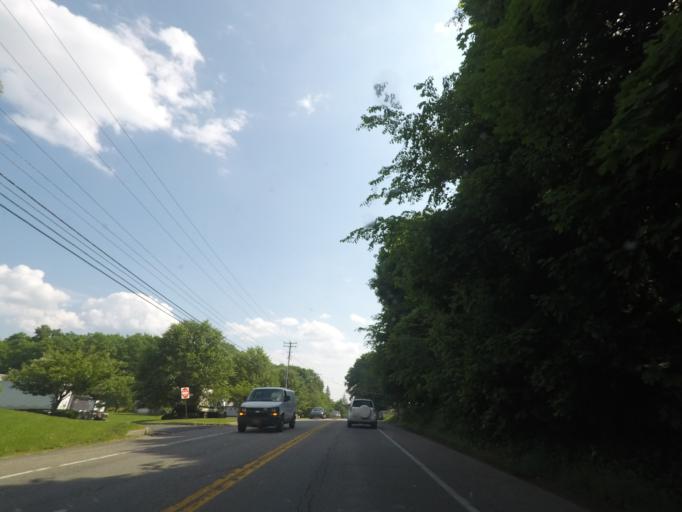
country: US
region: New York
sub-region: Ulster County
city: Marlboro
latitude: 41.5983
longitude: -73.9742
